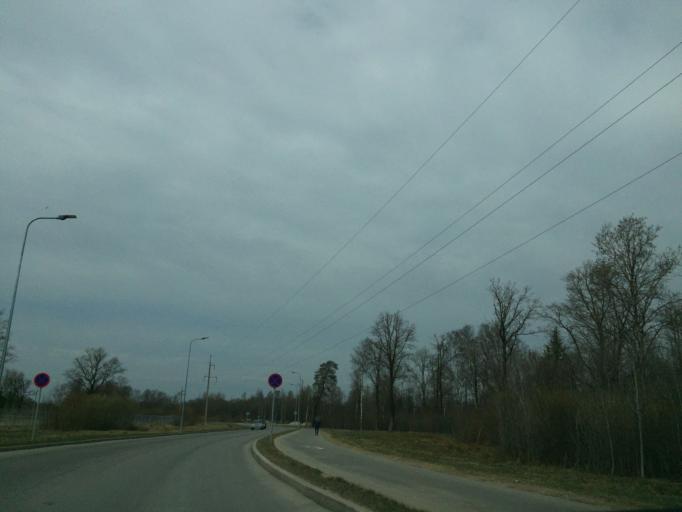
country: EE
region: Ida-Virumaa
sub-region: Narva linn
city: Narva
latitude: 59.3964
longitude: 28.1785
